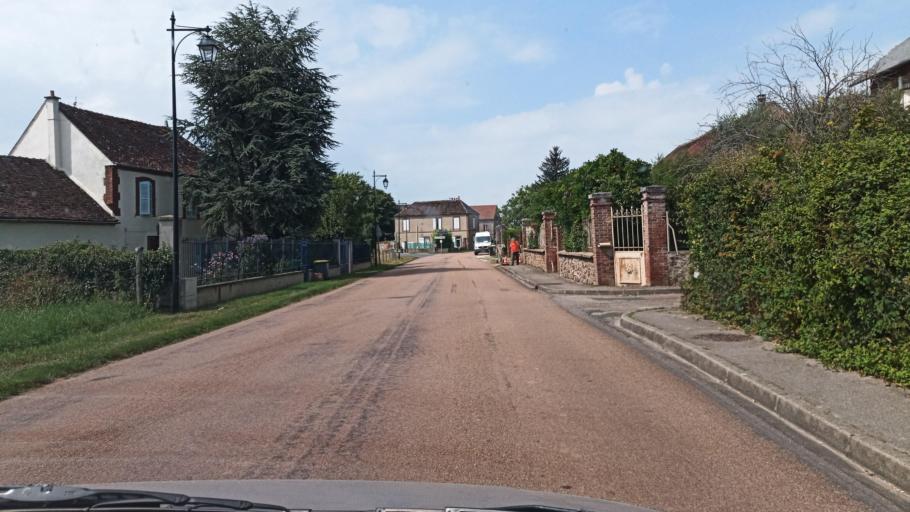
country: FR
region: Bourgogne
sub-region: Departement de l'Yonne
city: Saint-Julien-du-Sault
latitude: 48.0565
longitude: 3.2319
